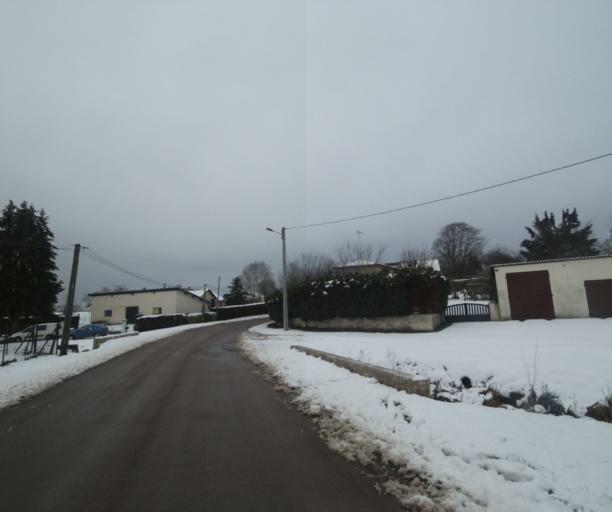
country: FR
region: Champagne-Ardenne
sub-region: Departement de la Haute-Marne
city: Laneuville-a-Remy
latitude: 48.5030
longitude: 4.8697
